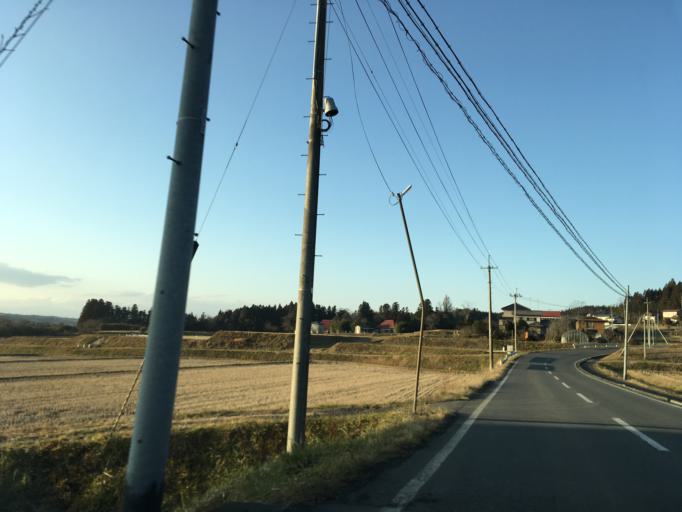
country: JP
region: Iwate
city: Ichinoseki
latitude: 38.8176
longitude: 141.2140
